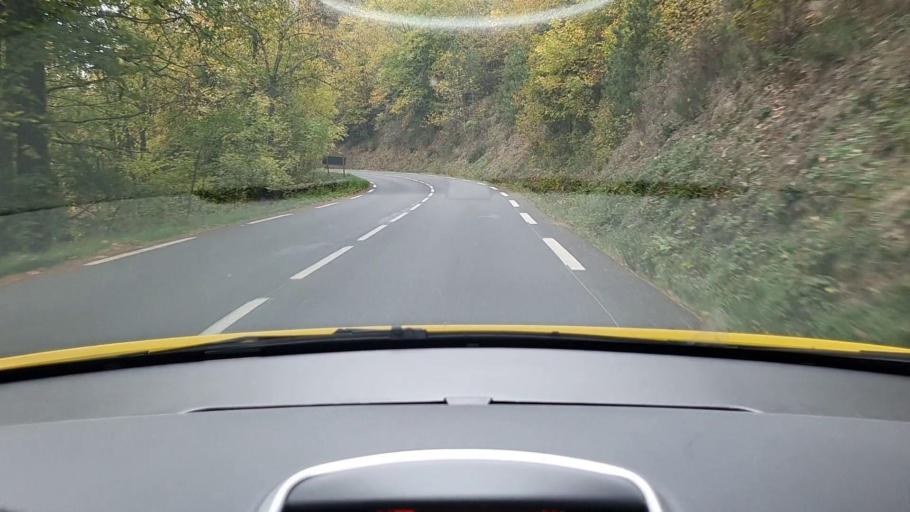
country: FR
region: Languedoc-Roussillon
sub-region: Departement de la Lozere
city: Meyrueis
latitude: 44.1304
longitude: 3.4194
